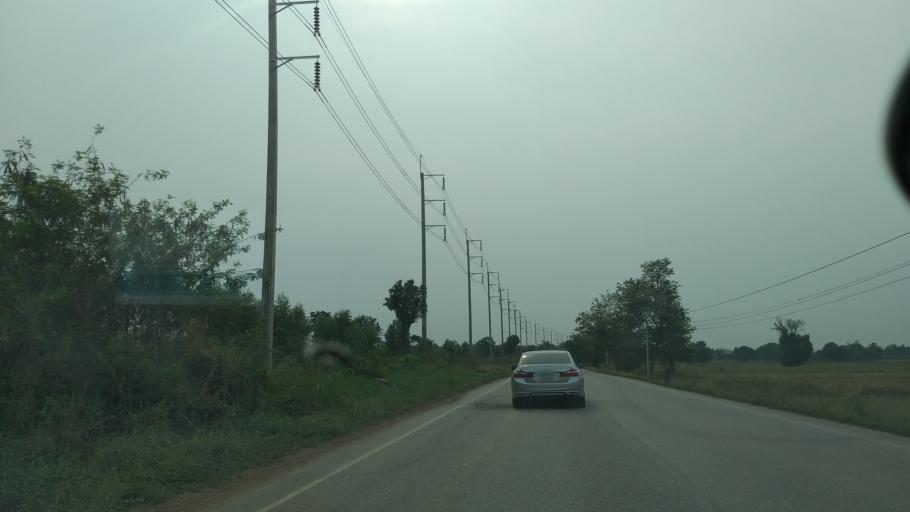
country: TH
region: Chachoengsao
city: Plaeng Yao
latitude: 13.5757
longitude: 101.2511
